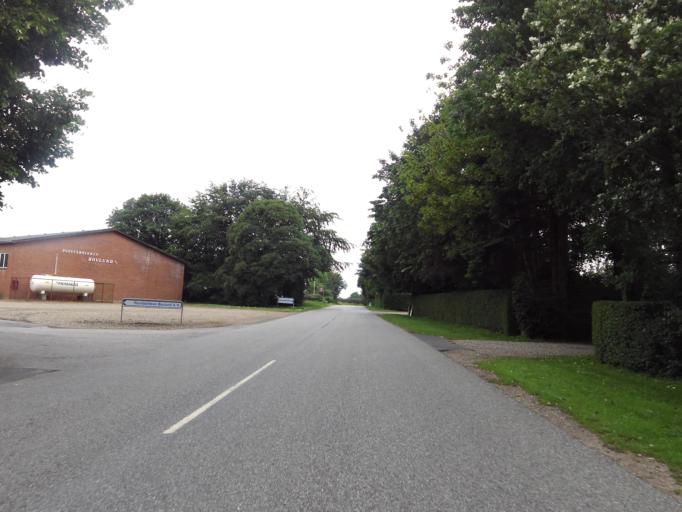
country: DK
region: South Denmark
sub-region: Tonder Kommune
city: Toftlund
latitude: 55.1016
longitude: 9.1040
